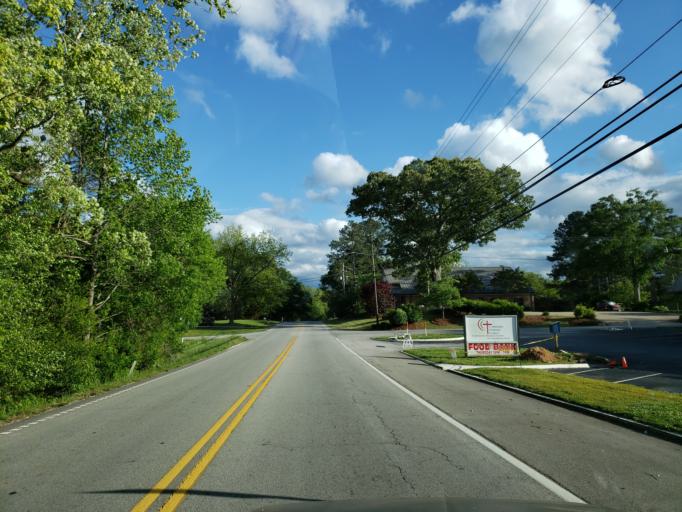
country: US
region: Georgia
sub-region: Haralson County
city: Tallapoosa
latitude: 33.7607
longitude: -85.2938
